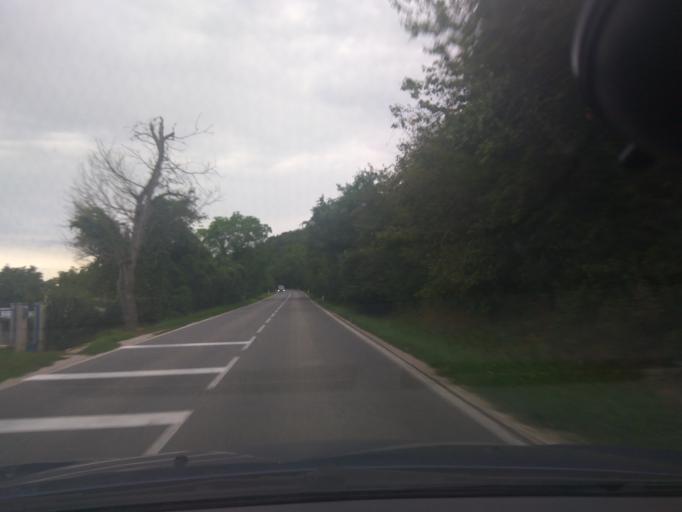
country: SK
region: Trnavsky
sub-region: Okres Trnava
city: Piestany
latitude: 48.6337
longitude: 17.8665
